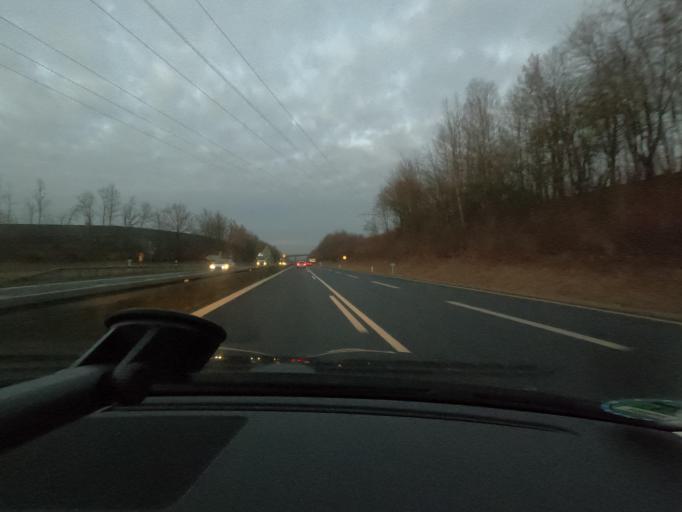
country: DE
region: Bavaria
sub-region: Upper Franconia
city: Bad Staffelstein
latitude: 50.0958
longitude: 11.0063
